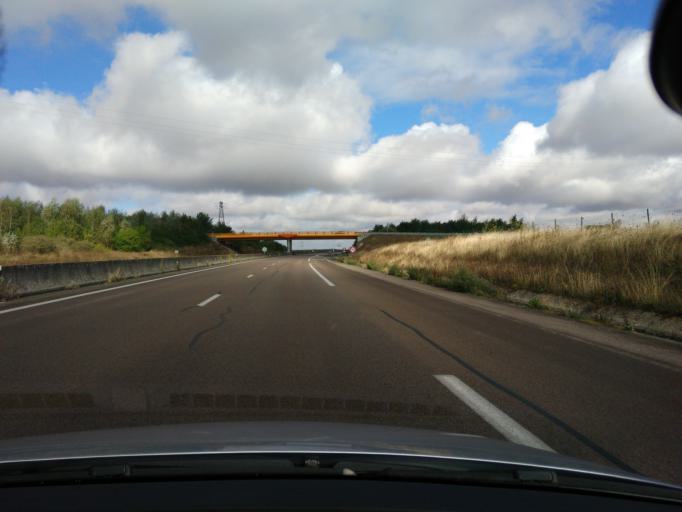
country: FR
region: Haute-Normandie
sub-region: Departement de l'Eure
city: La Madeleine-de-Nonancourt
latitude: 48.8335
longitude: 1.1839
